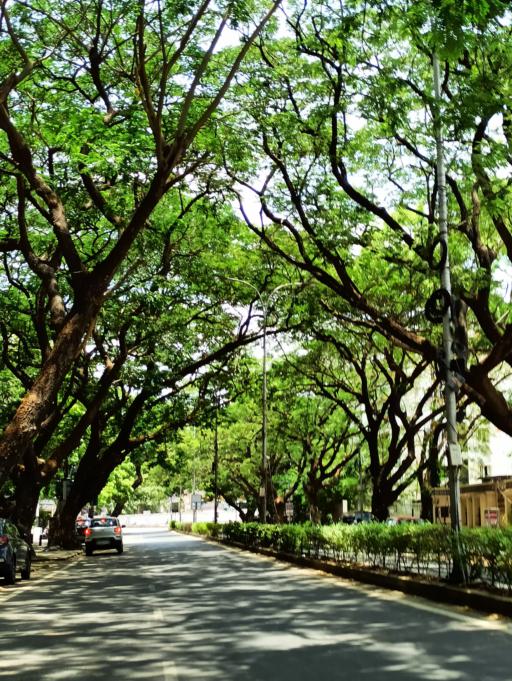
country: IN
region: Tamil Nadu
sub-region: Thiruvallur
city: Ambattur
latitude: 13.0829
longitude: 80.2000
